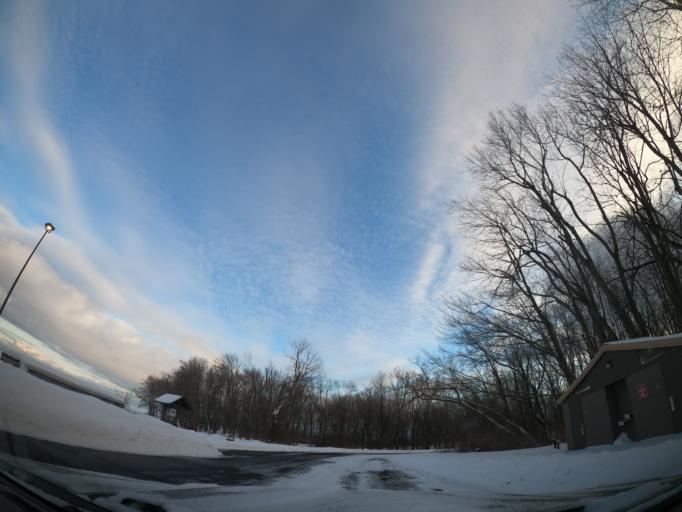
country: US
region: New York
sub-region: Onondaga County
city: Brewerton
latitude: 43.2279
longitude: -76.1089
